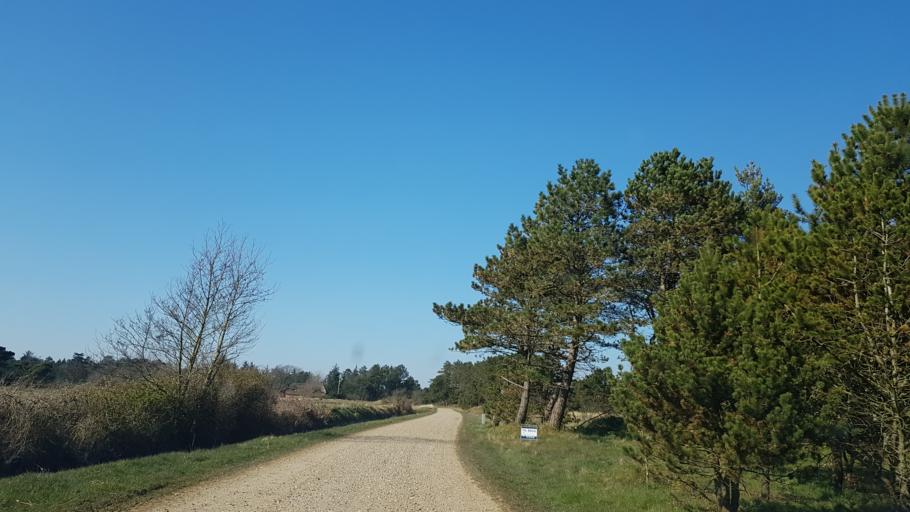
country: DE
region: Schleswig-Holstein
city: List
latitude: 55.0972
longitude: 8.5361
